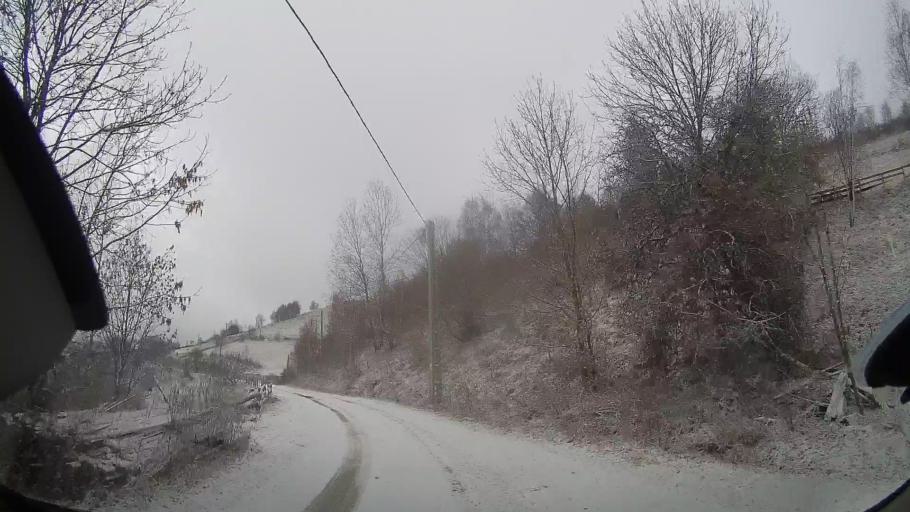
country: RO
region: Cluj
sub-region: Comuna Maguri-Racatau
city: Maguri-Racatau
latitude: 46.6648
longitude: 23.1839
